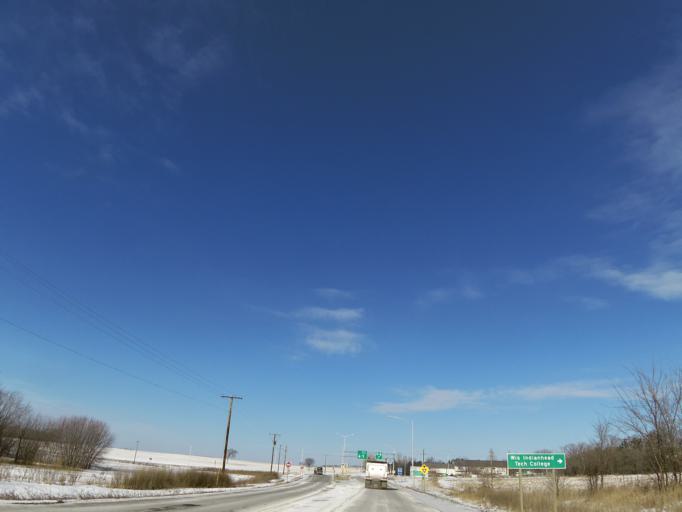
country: US
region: Wisconsin
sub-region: Saint Croix County
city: Roberts
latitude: 44.9902
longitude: -92.5580
